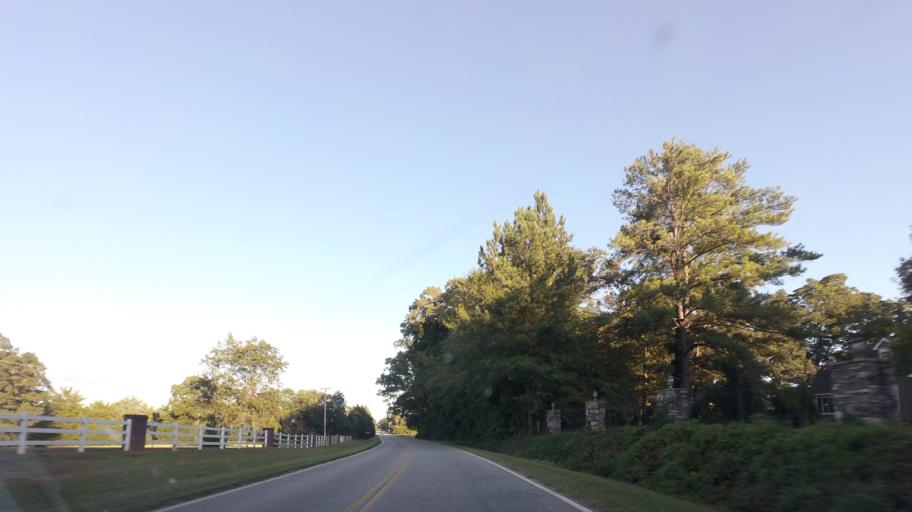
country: US
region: Georgia
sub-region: Spalding County
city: East Griffin
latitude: 33.2850
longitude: -84.1614
